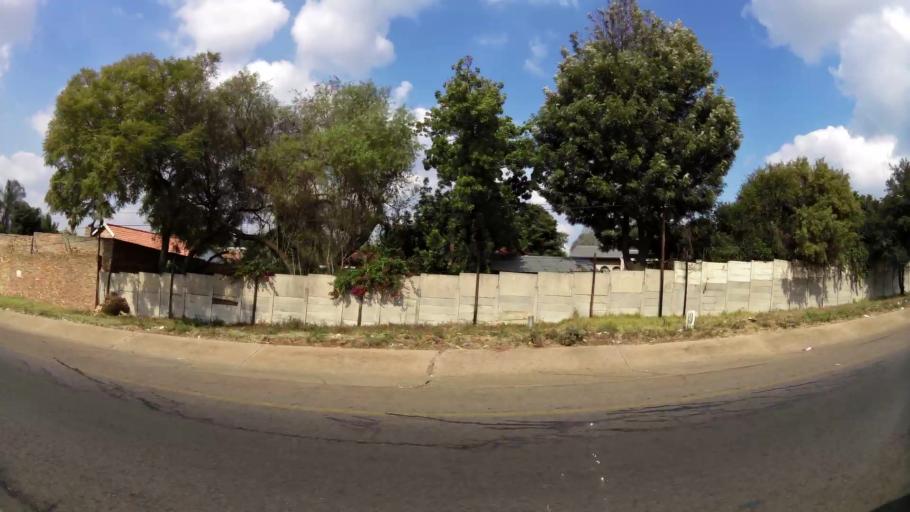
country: ZA
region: Gauteng
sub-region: City of Tshwane Metropolitan Municipality
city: Centurion
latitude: -25.8103
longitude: 28.2845
